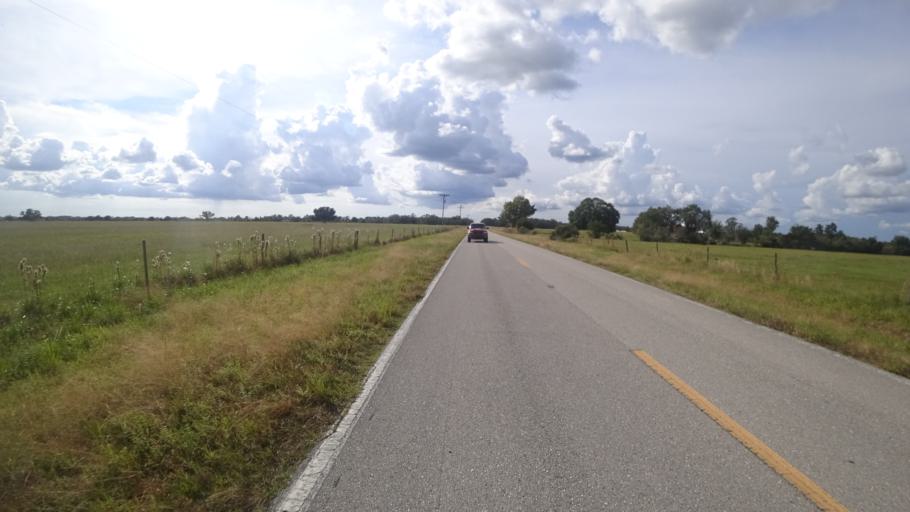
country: US
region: Florida
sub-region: Sarasota County
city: Lake Sarasota
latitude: 27.3390
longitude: -82.1813
